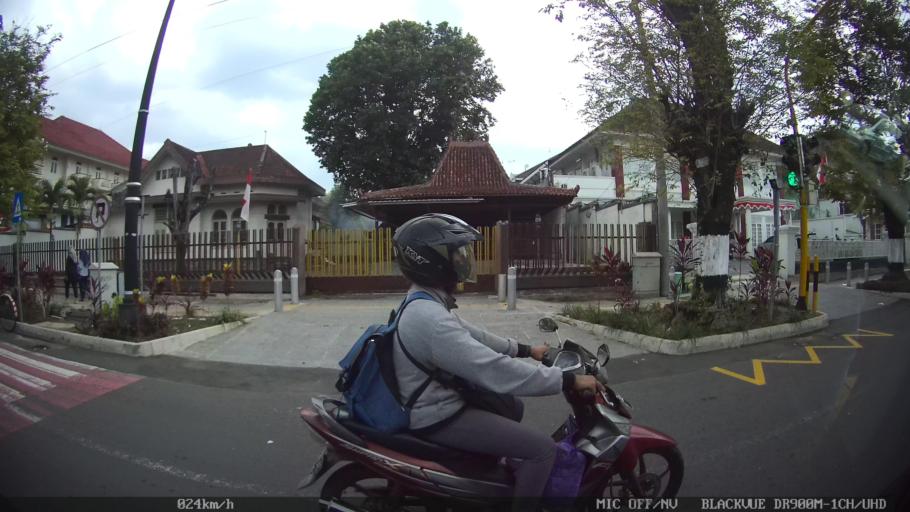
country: ID
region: Daerah Istimewa Yogyakarta
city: Yogyakarta
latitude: -7.7841
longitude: 110.3688
